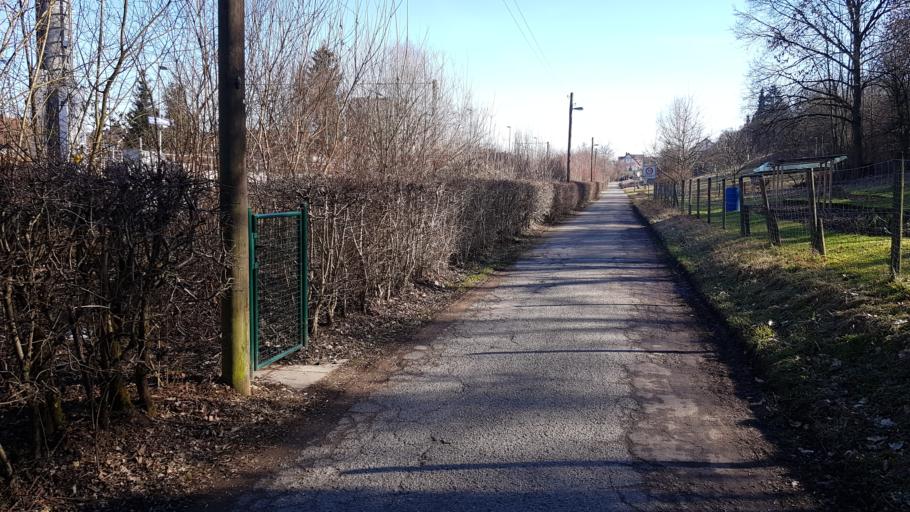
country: DE
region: Baden-Wuerttemberg
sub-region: Regierungsbezirk Stuttgart
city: Wernau
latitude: 48.6587
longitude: 9.4143
